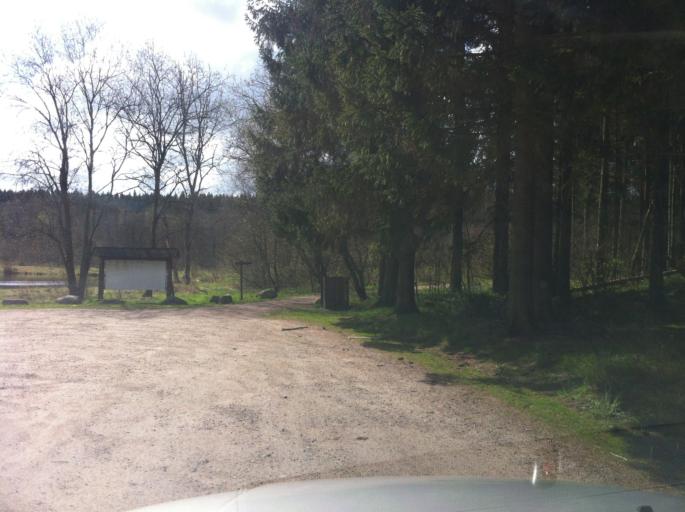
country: SE
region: Skane
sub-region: Hoors Kommun
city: Satofta
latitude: 55.9178
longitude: 13.6245
